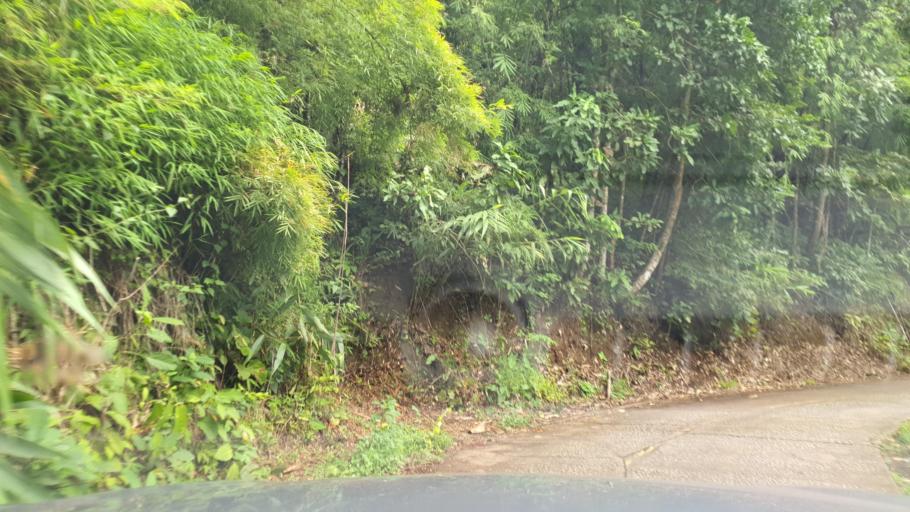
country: TH
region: Chiang Mai
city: Mae Taeng
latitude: 19.2259
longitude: 98.9244
